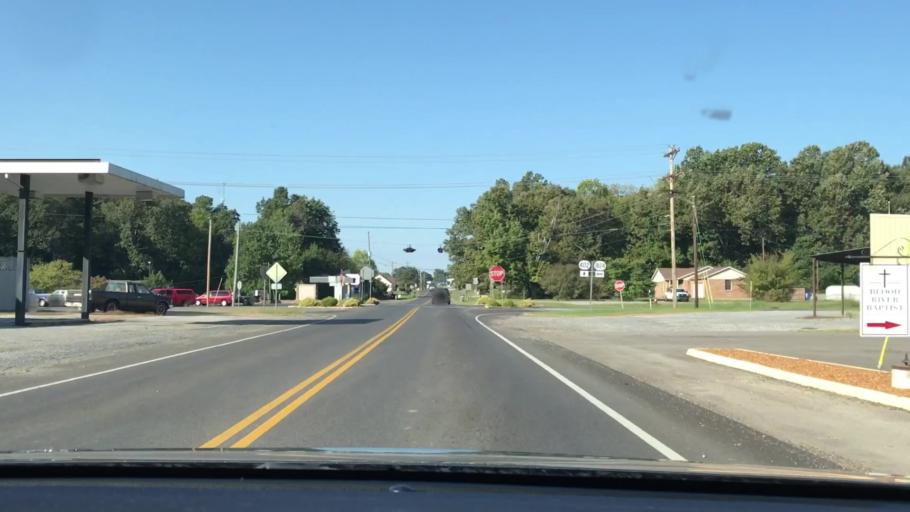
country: US
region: Kentucky
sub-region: Marshall County
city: Benton
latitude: 36.7668
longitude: -88.3033
